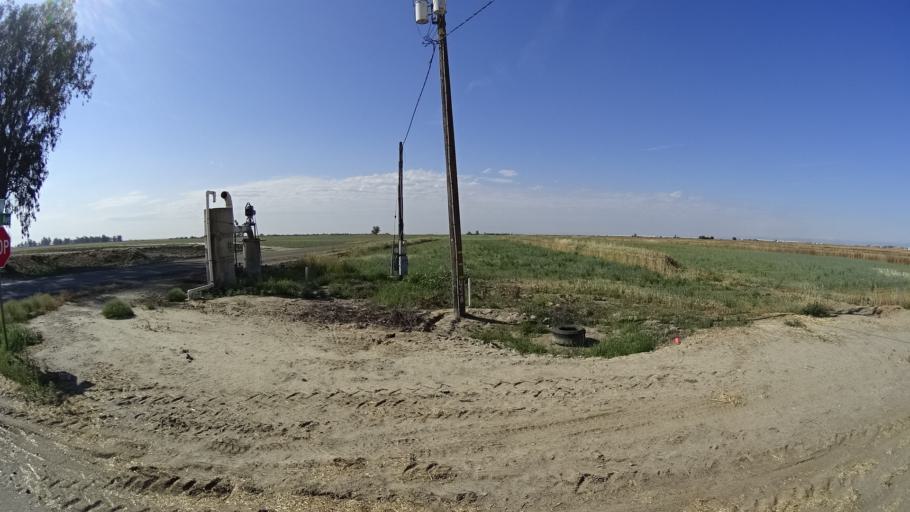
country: US
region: California
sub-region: Kings County
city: Home Garden
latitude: 36.2258
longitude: -119.6731
